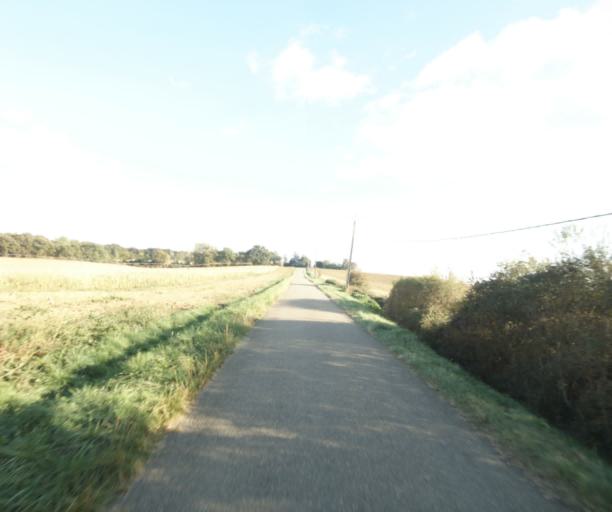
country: FR
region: Midi-Pyrenees
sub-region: Departement du Gers
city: Eauze
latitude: 43.7373
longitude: 0.1449
